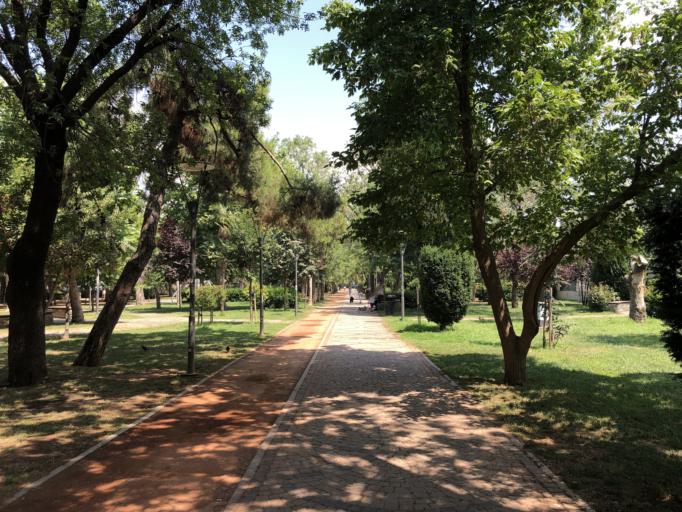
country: TR
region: Istanbul
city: UEskuedar
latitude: 40.9849
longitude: 29.0338
